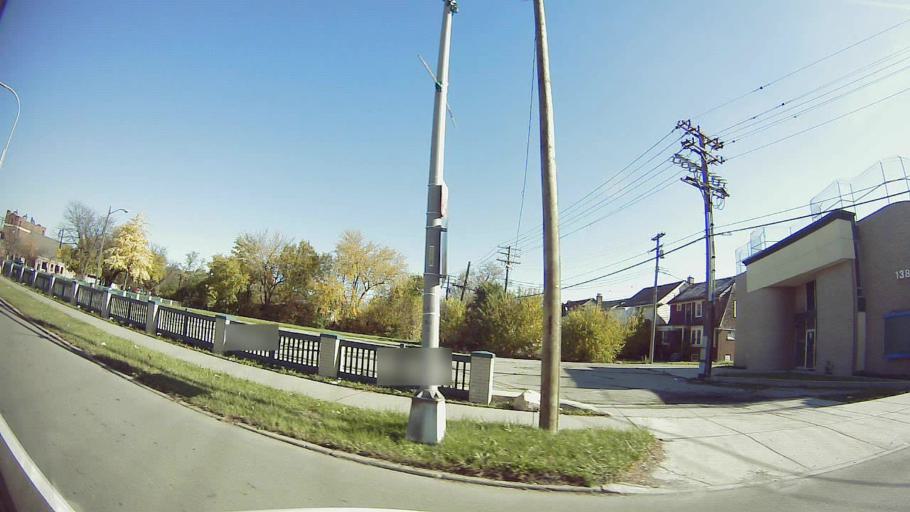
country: US
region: Michigan
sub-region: Wayne County
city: Highland Park
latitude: 42.3900
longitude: -83.1395
